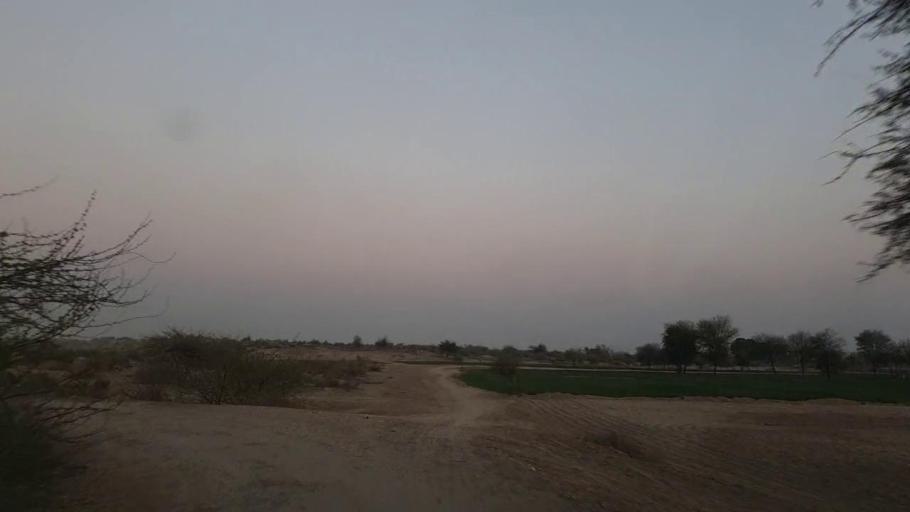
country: PK
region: Sindh
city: Bandhi
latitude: 26.6058
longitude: 68.3788
